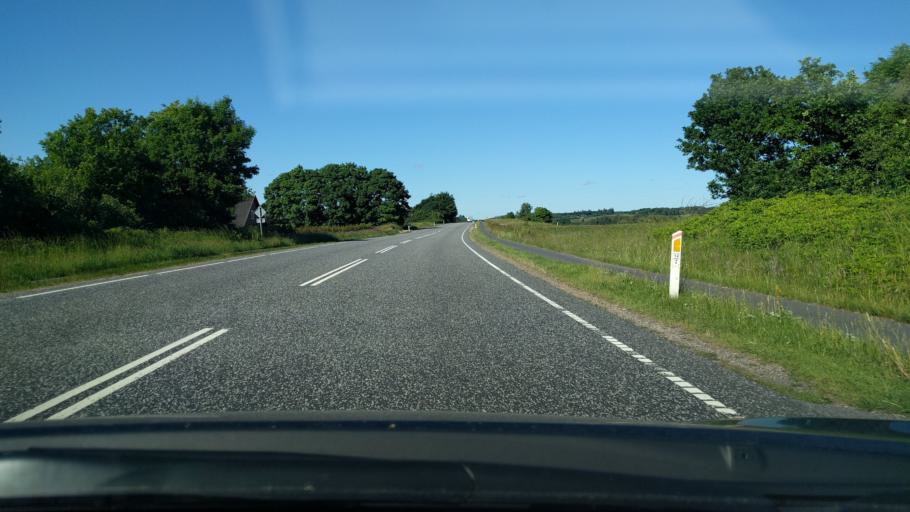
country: DK
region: North Denmark
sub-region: Vesthimmerland Kommune
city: Alestrup
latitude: 56.5677
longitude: 9.4852
